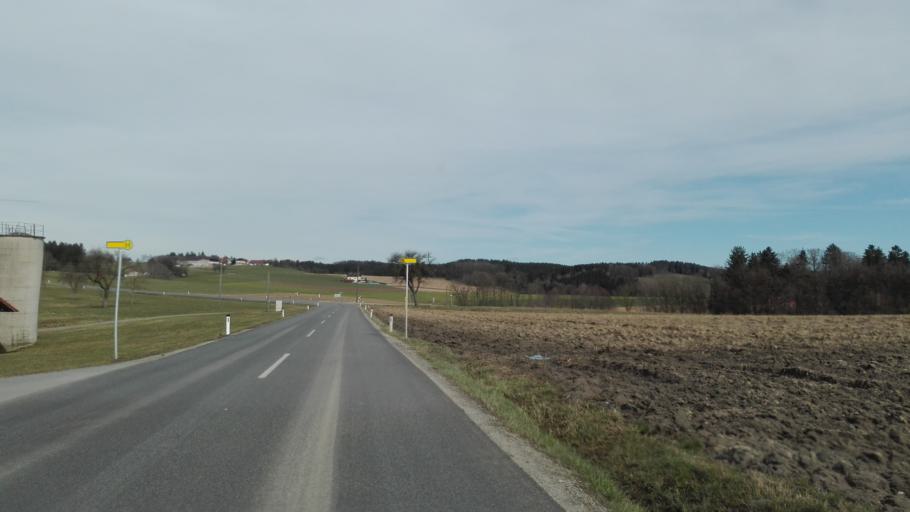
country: AT
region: Upper Austria
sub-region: Politischer Bezirk Scharding
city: Scharding
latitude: 48.5051
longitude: 13.4876
